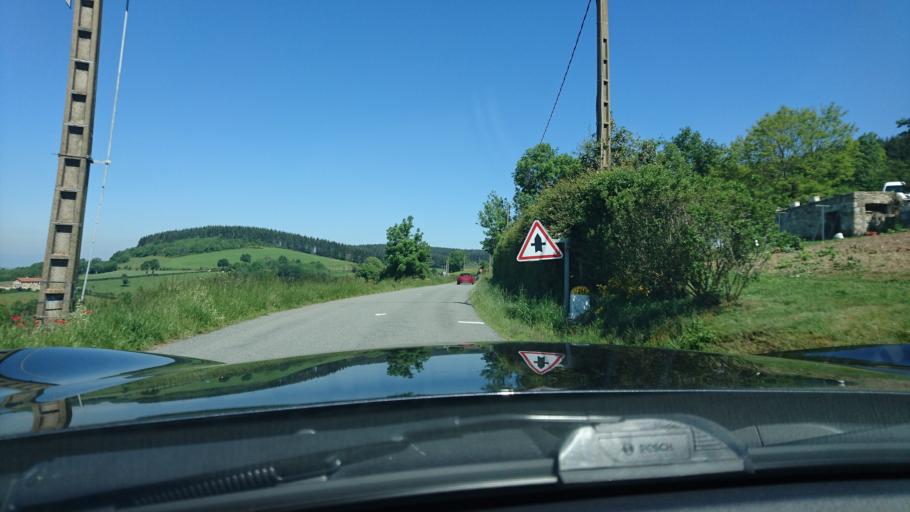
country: FR
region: Rhone-Alpes
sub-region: Departement de la Loire
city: Violay
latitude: 45.8885
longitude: 4.3311
